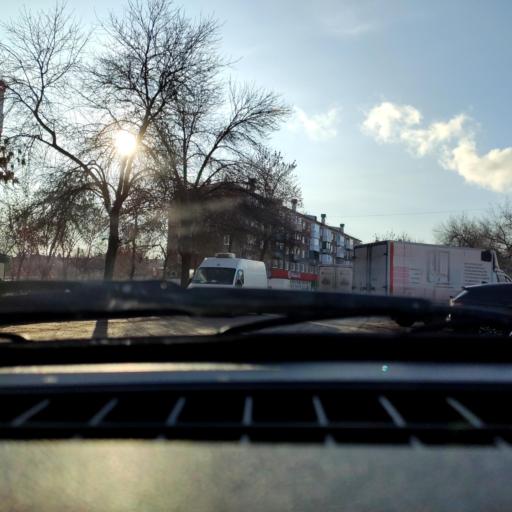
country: RU
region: Bashkortostan
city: Ufa
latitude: 54.8040
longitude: 56.1257
